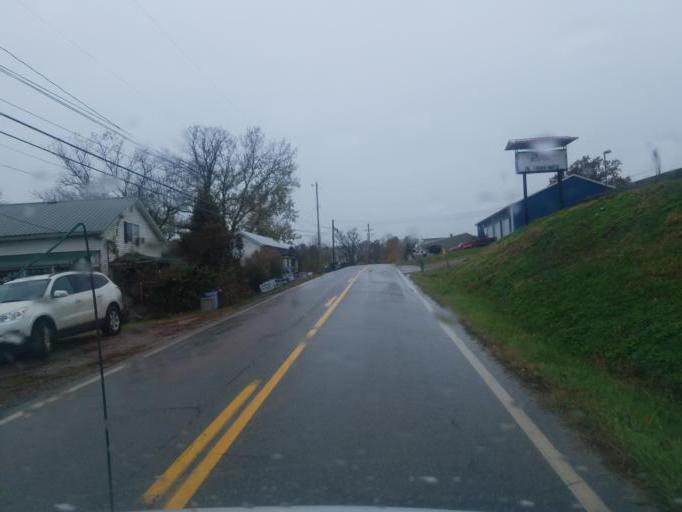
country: US
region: Ohio
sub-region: Washington County
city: Beverly
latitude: 39.4657
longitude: -81.6318
